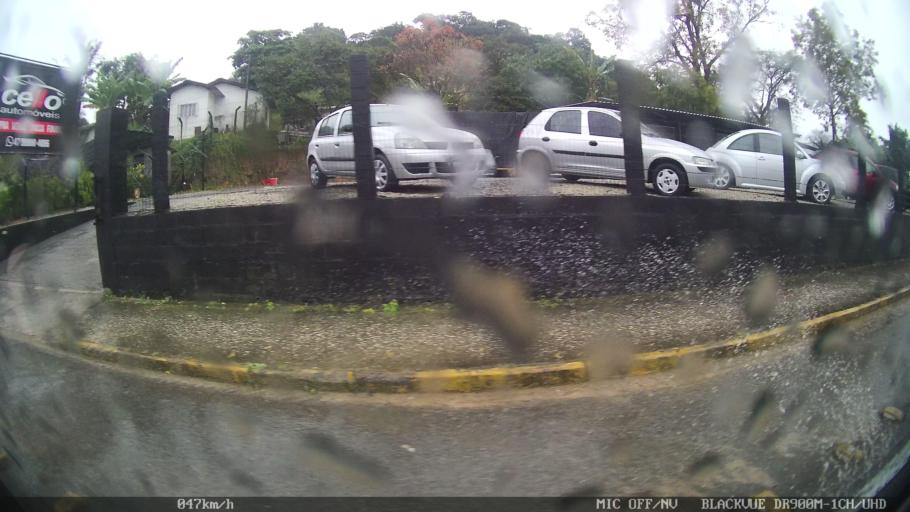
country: BR
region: Santa Catarina
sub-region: Balneario Camboriu
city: Balneario Camboriu
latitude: -27.0135
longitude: -48.6487
